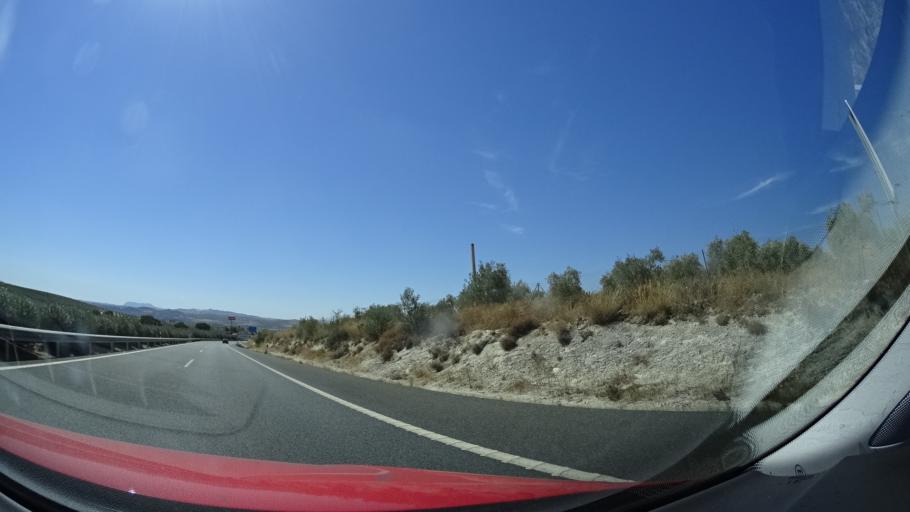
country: ES
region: Andalusia
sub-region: Provincia de Sevilla
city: Aguadulce
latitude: 37.2683
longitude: -4.9534
